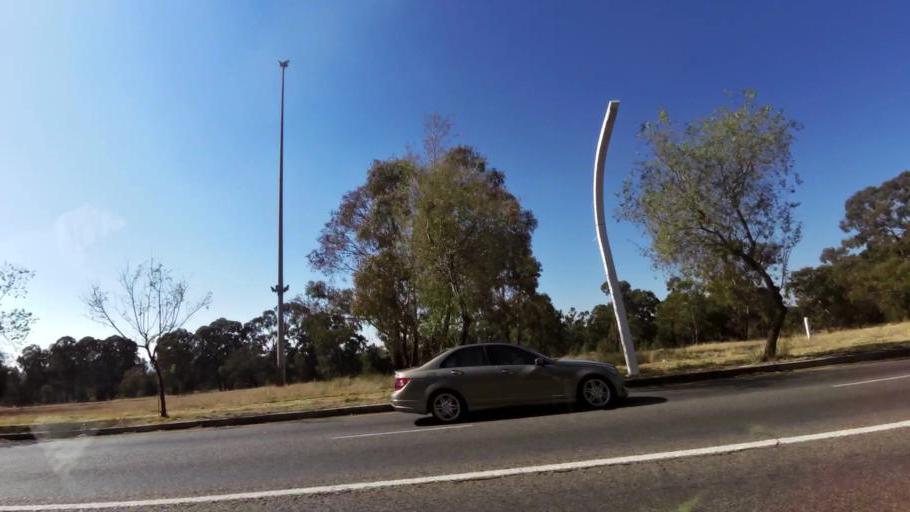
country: ZA
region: Gauteng
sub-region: City of Johannesburg Metropolitan Municipality
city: Johannesburg
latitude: -26.2421
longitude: 27.9855
